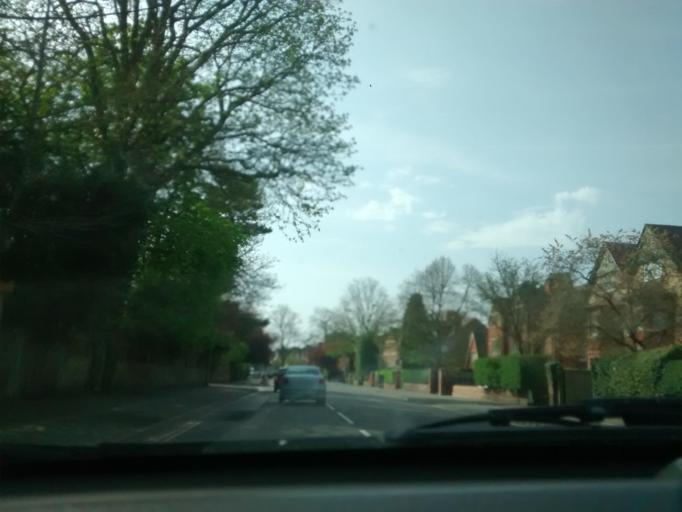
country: GB
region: England
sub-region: Oxfordshire
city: Oxford
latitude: 51.7725
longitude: -1.2669
